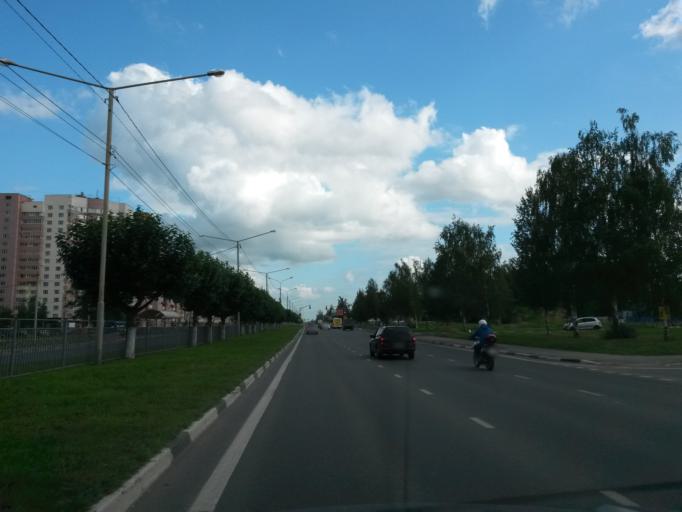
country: RU
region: Jaroslavl
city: Yaroslavl
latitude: 57.5852
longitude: 39.9064
